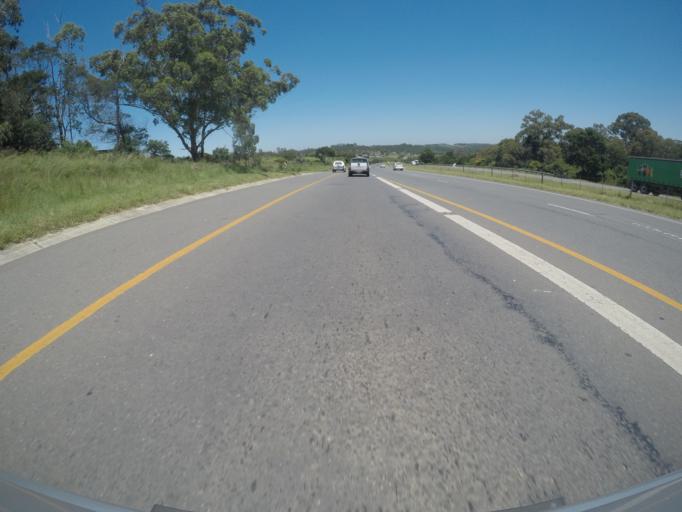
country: ZA
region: Eastern Cape
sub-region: Buffalo City Metropolitan Municipality
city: East London
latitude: -32.9402
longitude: 27.9485
